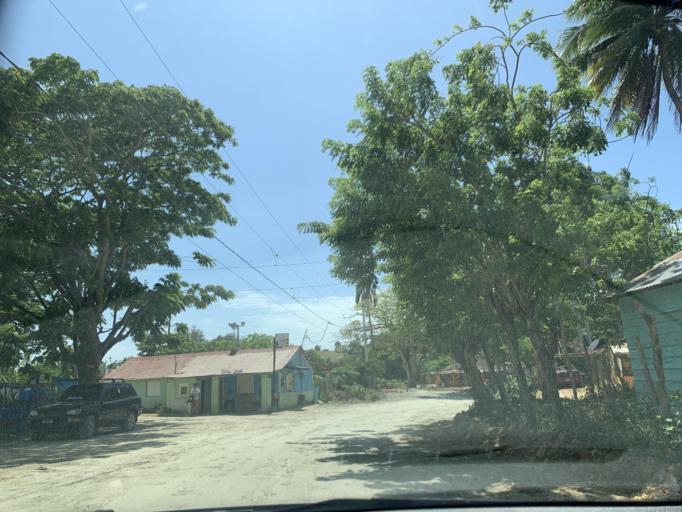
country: DO
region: Puerto Plata
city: Luperon
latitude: 19.8825
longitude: -70.8372
